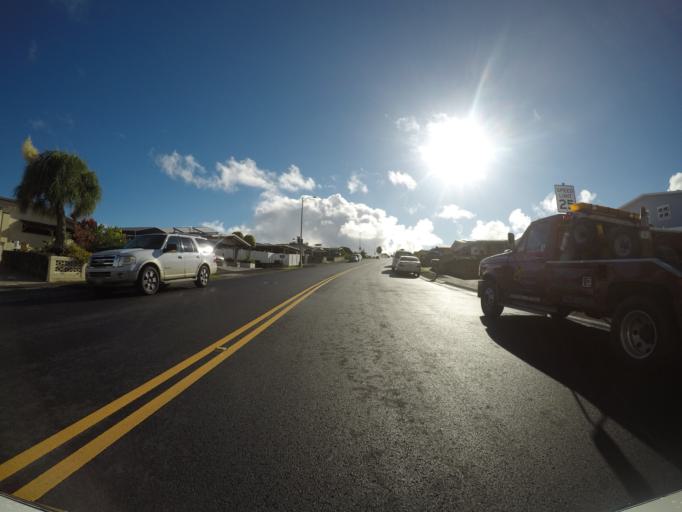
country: US
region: Hawaii
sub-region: Honolulu County
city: He'eia
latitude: 21.4233
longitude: -157.8098
